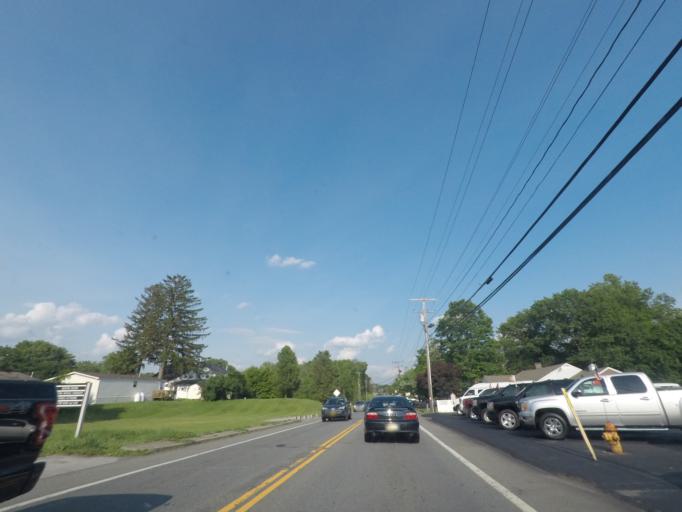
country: US
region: New York
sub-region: Orange County
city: Vails Gate
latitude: 41.4864
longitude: -74.0894
